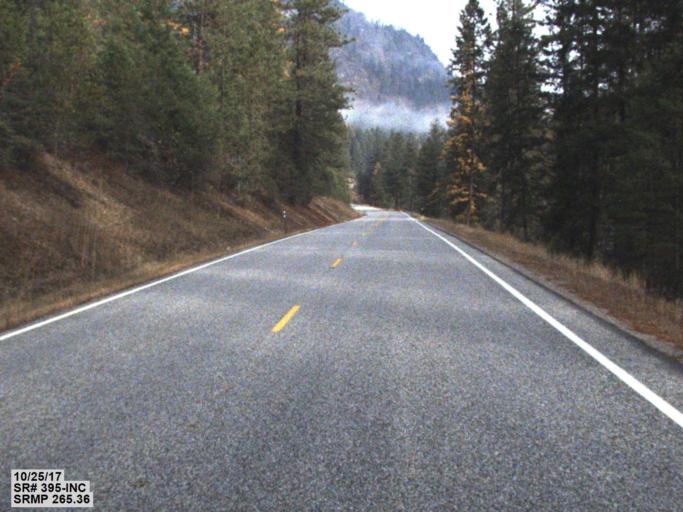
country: CA
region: British Columbia
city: Grand Forks
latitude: 48.9323
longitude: -118.2202
